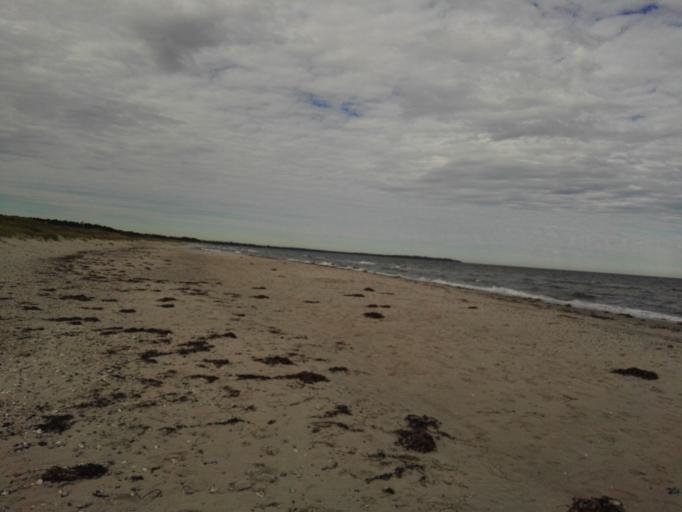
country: DK
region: Zealand
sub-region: Odsherred Kommune
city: Nykobing Sjaelland
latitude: 55.9480
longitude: 11.7000
